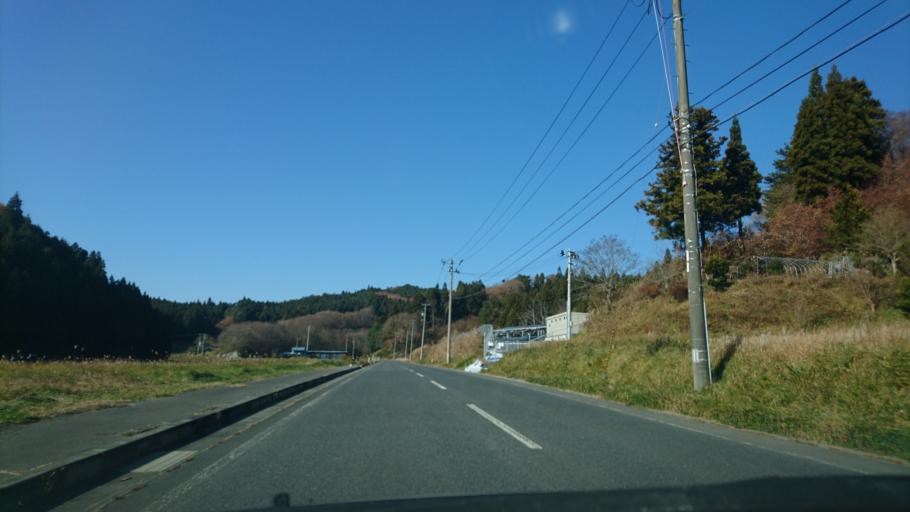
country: JP
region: Iwate
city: Ichinoseki
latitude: 38.9025
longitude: 141.4184
